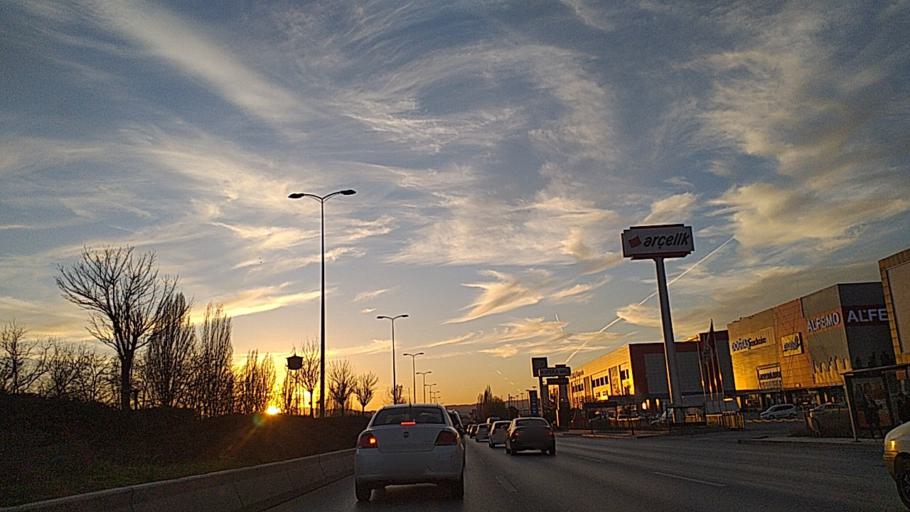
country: TR
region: Ankara
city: Etimesgut
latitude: 39.9631
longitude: 32.6548
